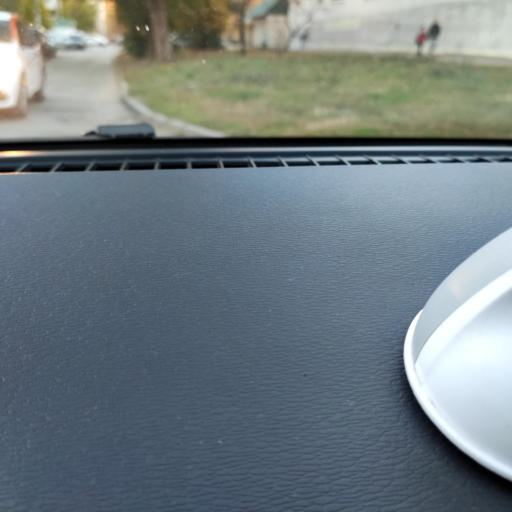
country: RU
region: Samara
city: Samara
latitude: 53.2558
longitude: 50.2254
